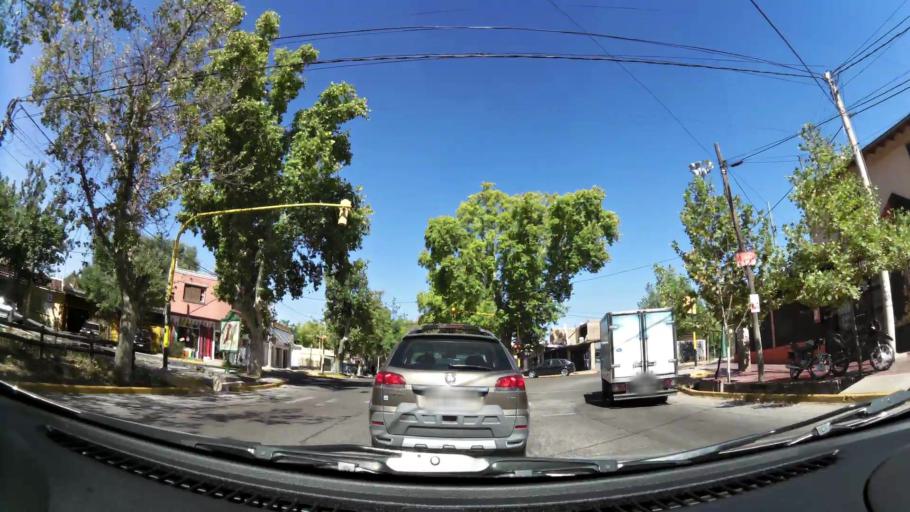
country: AR
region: Mendoza
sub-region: Departamento de Godoy Cruz
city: Godoy Cruz
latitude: -32.9558
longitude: -68.8501
